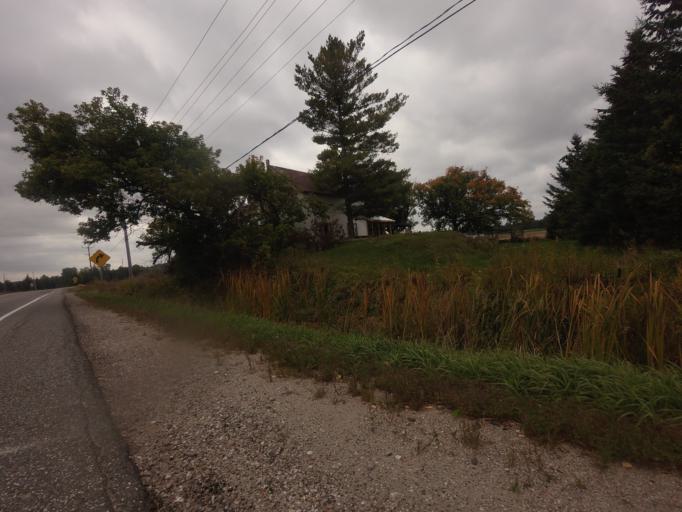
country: CA
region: Quebec
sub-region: Outaouais
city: Wakefield
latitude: 45.9136
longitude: -76.0170
